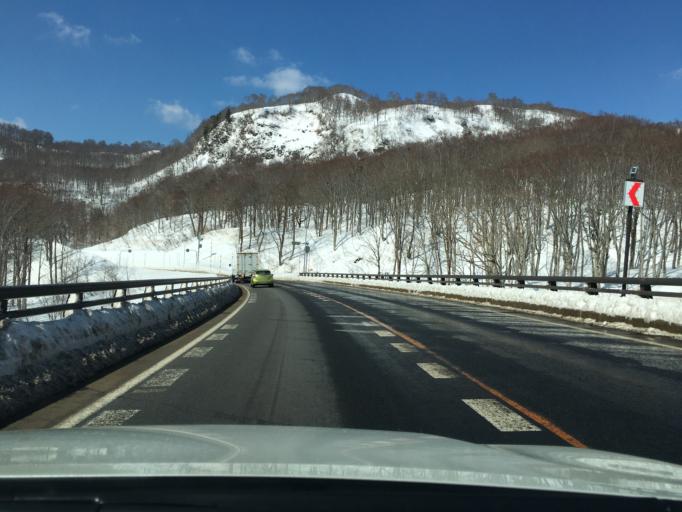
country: JP
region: Yamagata
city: Tsuruoka
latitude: 38.5316
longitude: 139.9501
